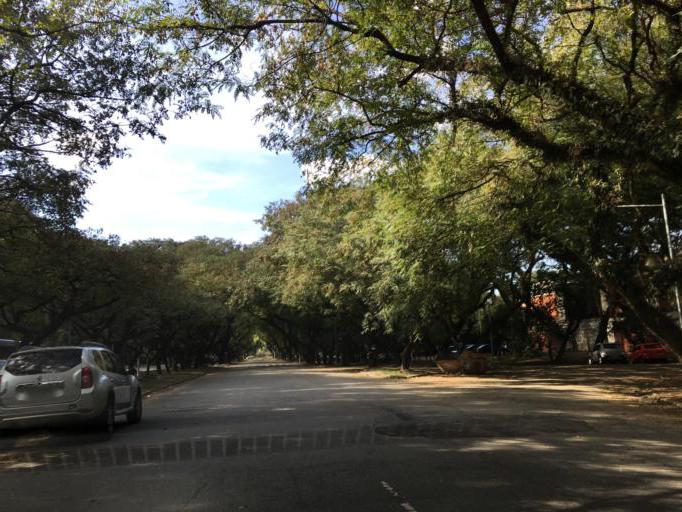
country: BR
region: Sao Paulo
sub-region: Osasco
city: Osasco
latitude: -23.5569
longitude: -46.7265
